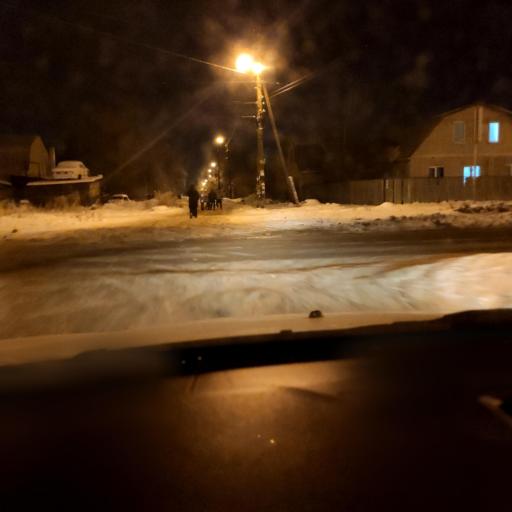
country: RU
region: Samara
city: Smyshlyayevka
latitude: 53.2464
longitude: 50.3379
